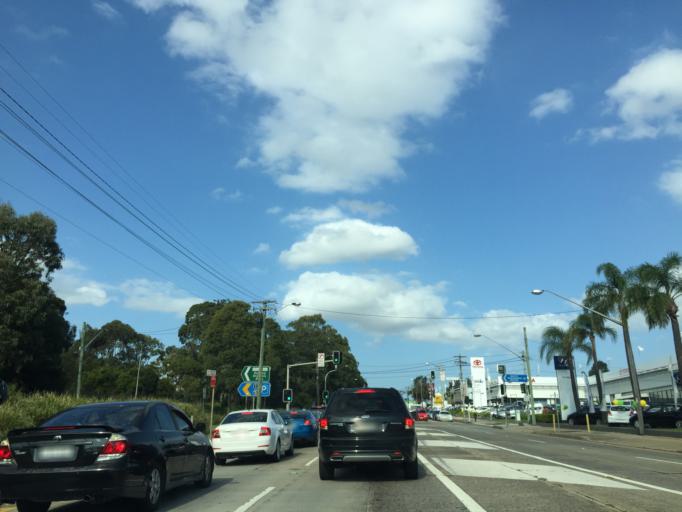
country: AU
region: New South Wales
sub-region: Auburn
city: Lidcombe
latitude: -33.8504
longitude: 151.0530
